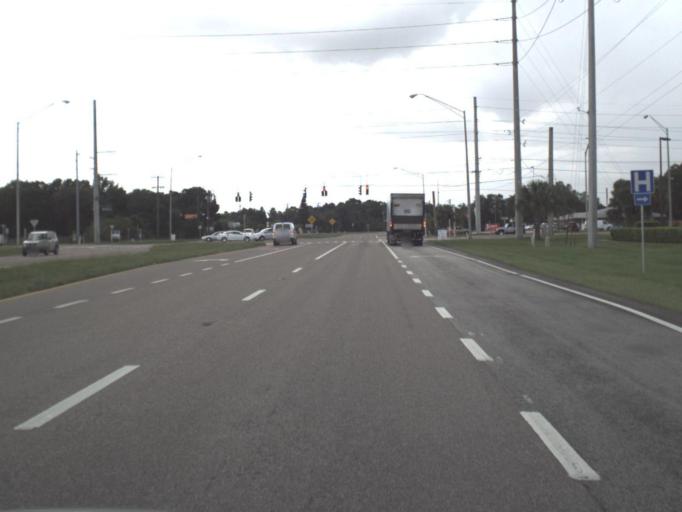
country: US
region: Florida
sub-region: Hillsborough County
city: Sun City Center
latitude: 27.7137
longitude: -82.3353
